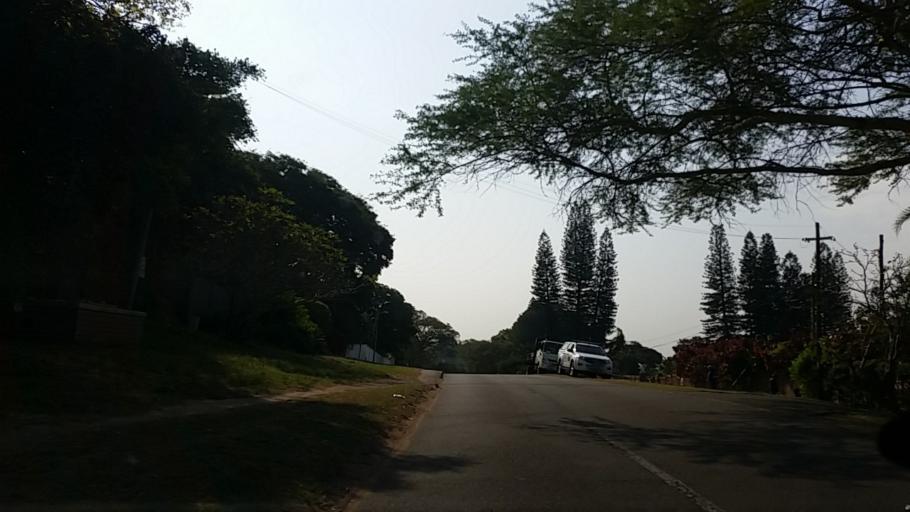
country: ZA
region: KwaZulu-Natal
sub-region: eThekwini Metropolitan Municipality
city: Berea
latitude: -29.8403
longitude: 30.9405
